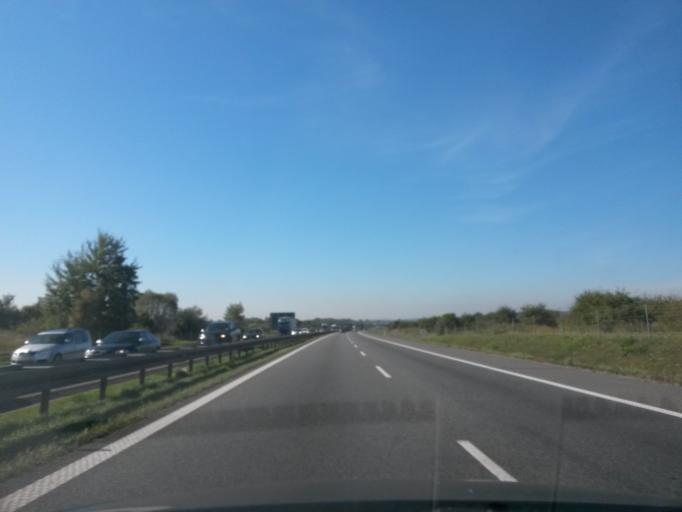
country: PL
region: Lesser Poland Voivodeship
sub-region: Powiat krakowski
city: Libertow
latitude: 49.9906
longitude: 19.8994
